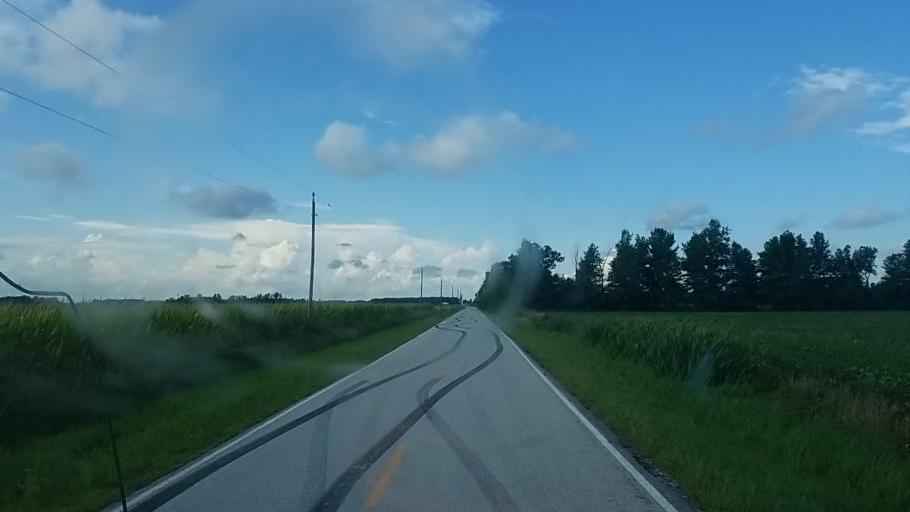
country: US
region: Ohio
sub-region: Hardin County
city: Forest
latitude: 40.7546
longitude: -83.4967
